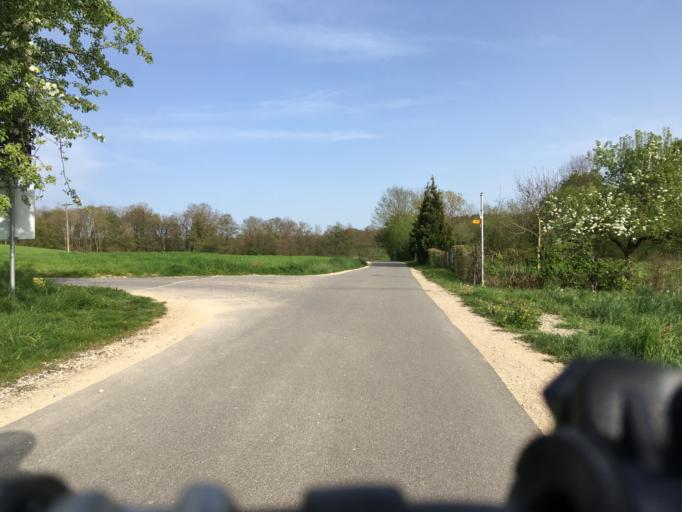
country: DE
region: Baden-Wuerttemberg
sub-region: Freiburg Region
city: Gailingen
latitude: 47.6870
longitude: 8.7683
